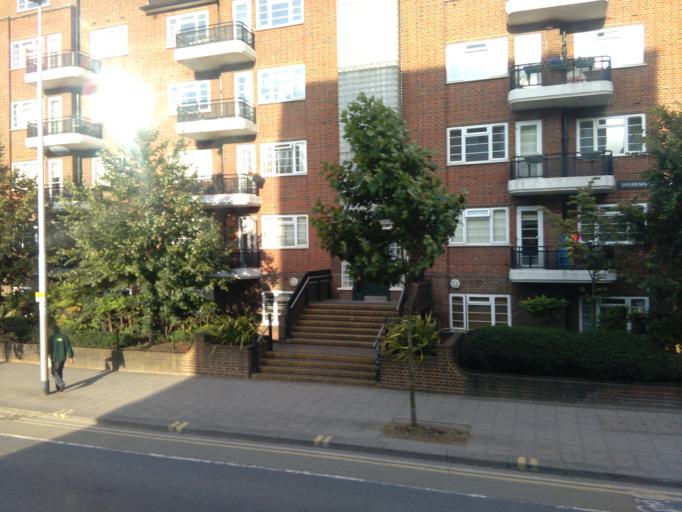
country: GB
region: England
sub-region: Greater London
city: City of Westminster
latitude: 51.4789
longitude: -0.1289
